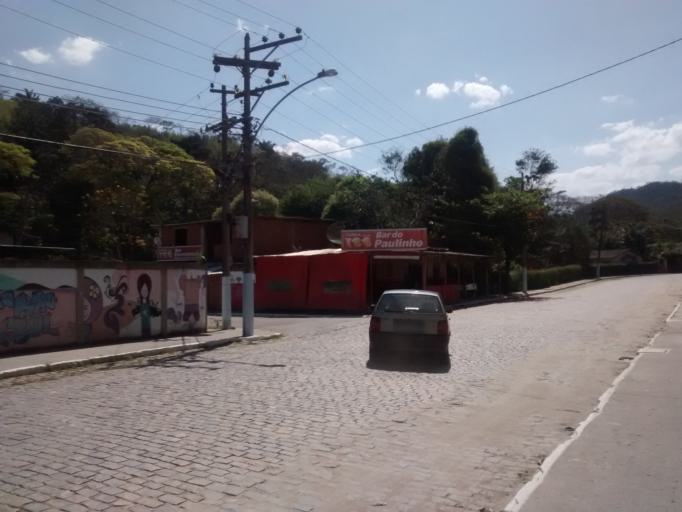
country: BR
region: Rio de Janeiro
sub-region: Vassouras
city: Vassouras
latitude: -22.4751
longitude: -43.5824
